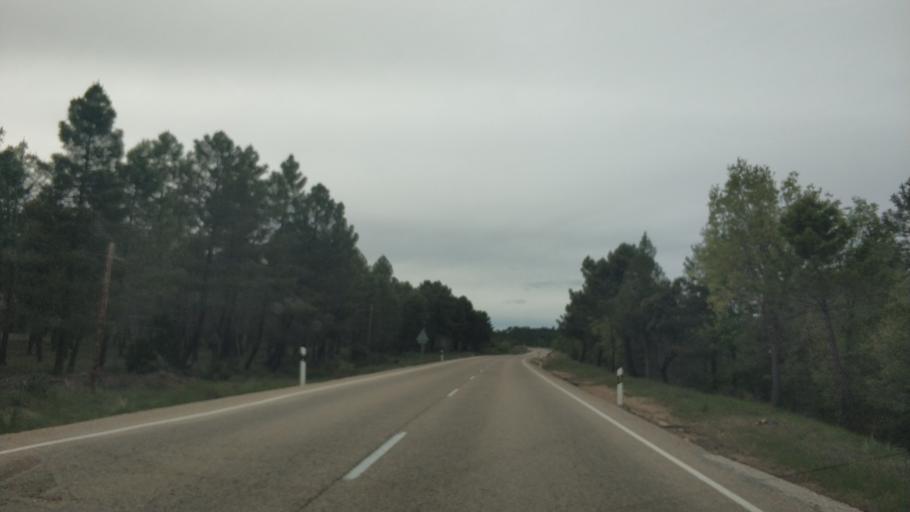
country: ES
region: Castille and Leon
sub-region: Provincia de Soria
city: Bayubas de Abajo
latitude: 41.5153
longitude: -2.9278
